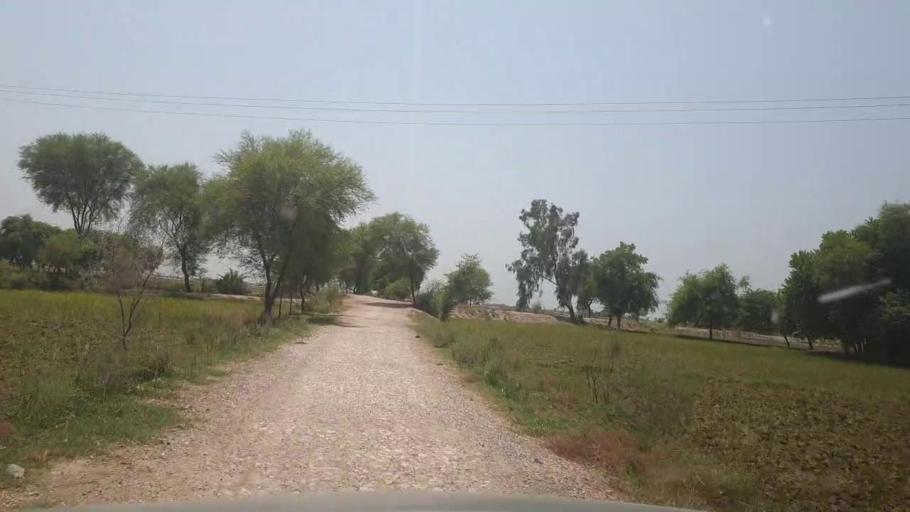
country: PK
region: Sindh
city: Lakhi
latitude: 27.8458
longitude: 68.6640
